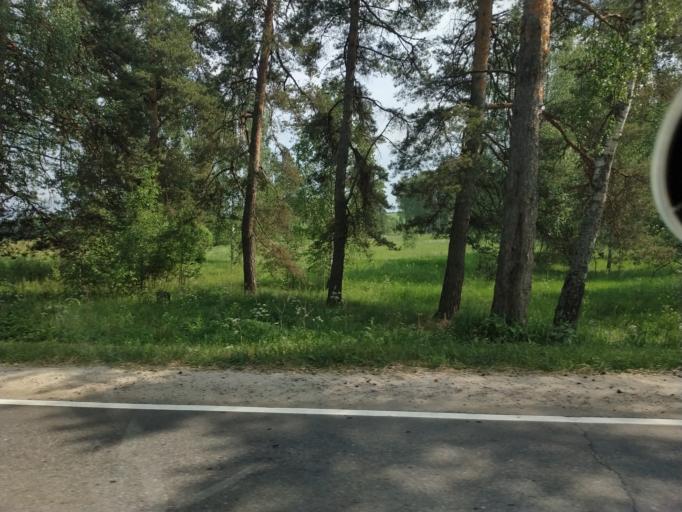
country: RU
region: Moskovskaya
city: Zhilevo
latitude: 55.0547
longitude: 38.0442
